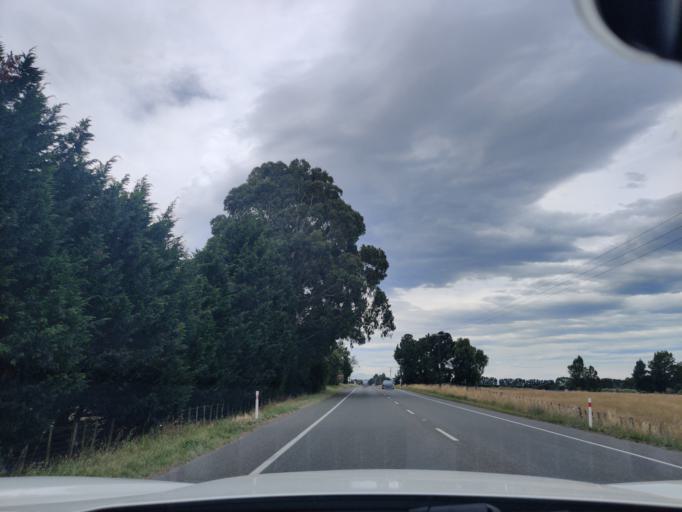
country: NZ
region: Wellington
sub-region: Masterton District
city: Masterton
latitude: -40.9843
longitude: 175.5803
